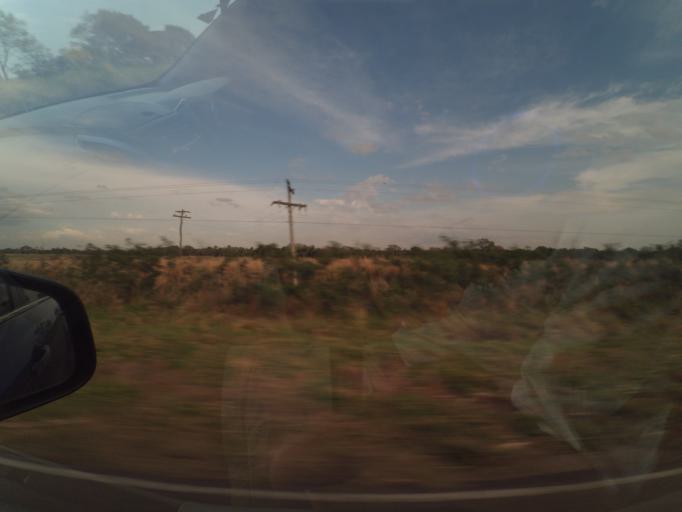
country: BO
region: Santa Cruz
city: Okinawa Numero Uno
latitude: -17.2314
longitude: -62.9397
